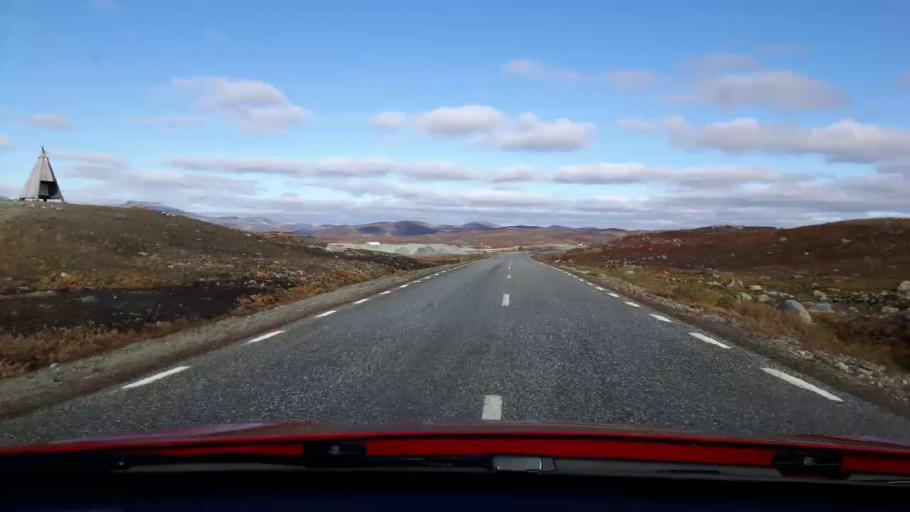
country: NO
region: Nordland
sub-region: Hattfjelldal
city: Hattfjelldal
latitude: 65.0879
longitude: 14.4588
